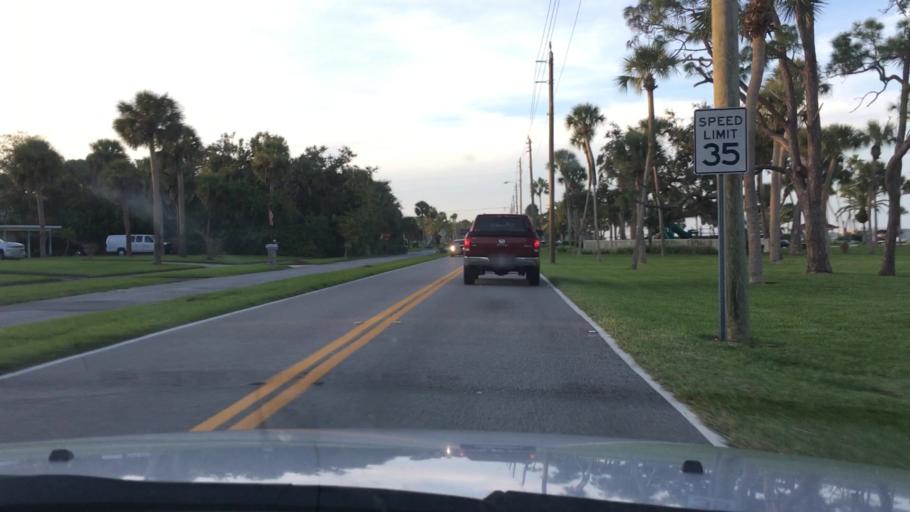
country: US
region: Florida
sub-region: Volusia County
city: Holly Hill
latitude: 29.2626
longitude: -81.0440
